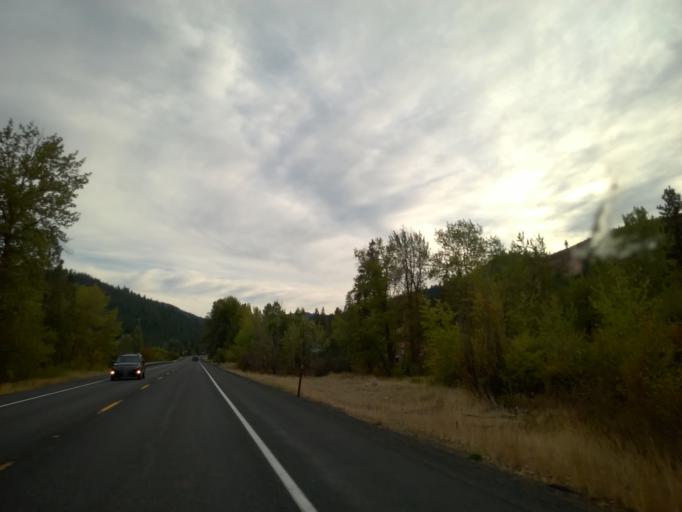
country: US
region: Washington
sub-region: Chelan County
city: Leavenworth
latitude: 47.5211
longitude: -120.6258
